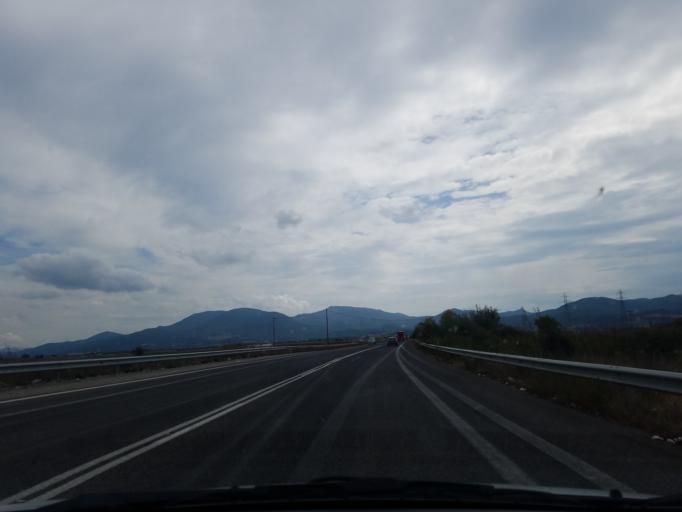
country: GR
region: Central Greece
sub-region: Nomos Fthiotidos
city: Domokos
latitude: 39.0537
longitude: 22.3400
